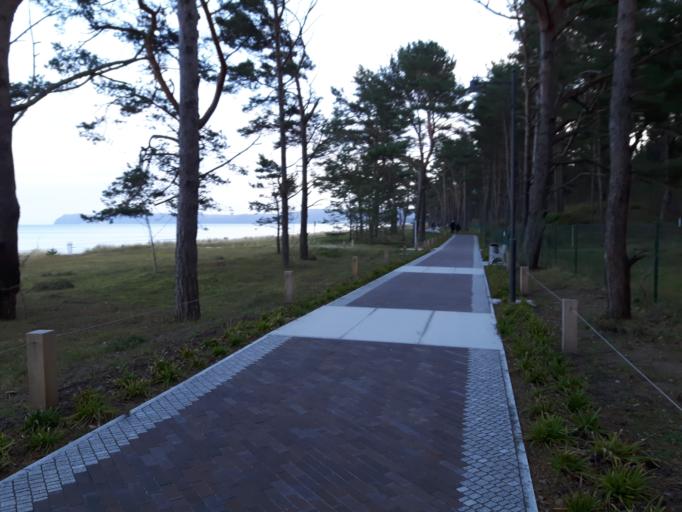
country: DE
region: Mecklenburg-Vorpommern
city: Ostseebad Binz
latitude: 54.4211
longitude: 13.5906
